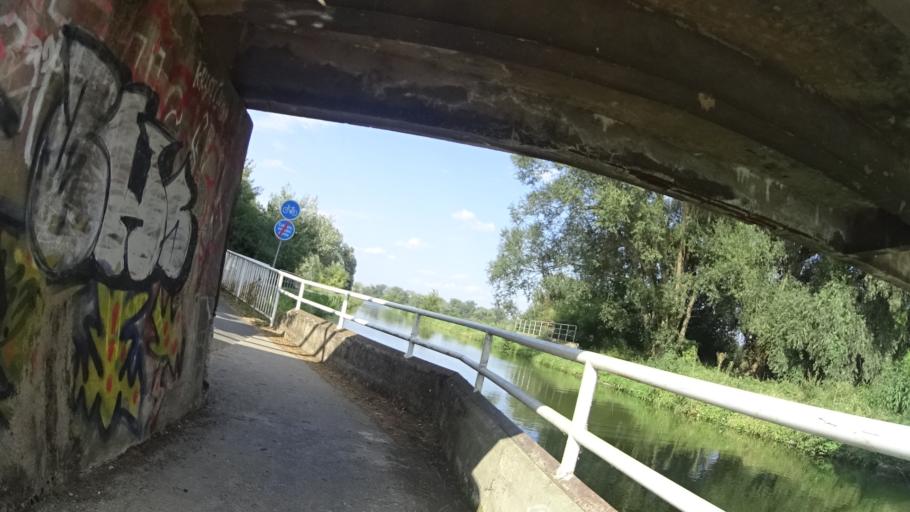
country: CZ
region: Zlin
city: Babice
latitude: 49.1247
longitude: 17.4925
